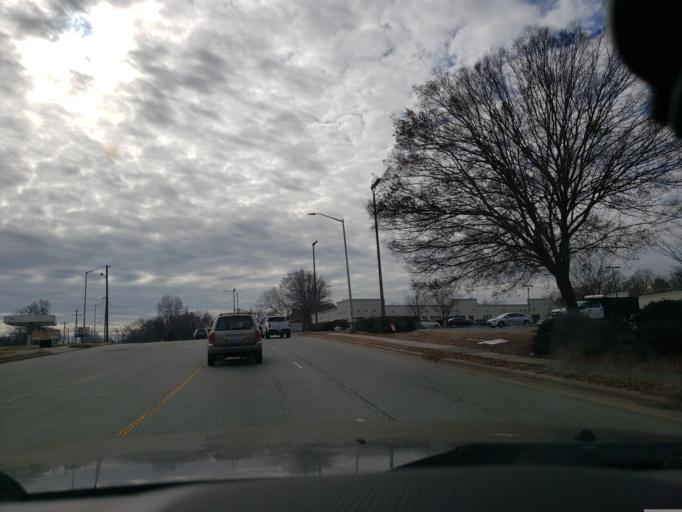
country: US
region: North Carolina
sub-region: Durham County
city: Durham
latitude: 35.9854
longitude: -78.8989
